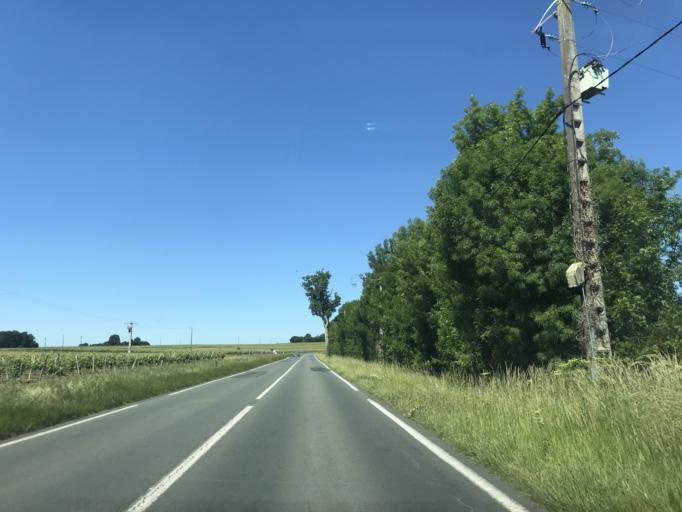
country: FR
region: Poitou-Charentes
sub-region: Departement de la Charente-Maritime
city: Gemozac
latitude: 45.5713
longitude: -0.6208
